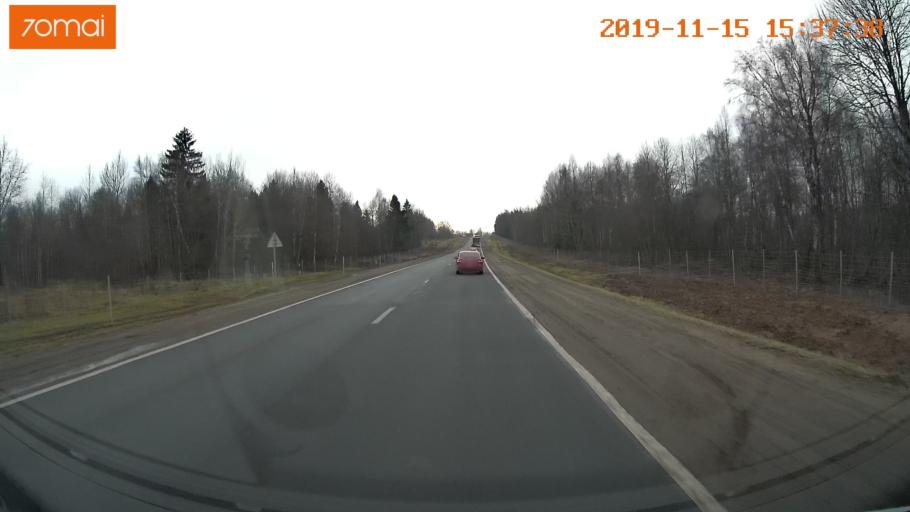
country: RU
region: Jaroslavl
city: Danilov
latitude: 58.0375
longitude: 40.0876
